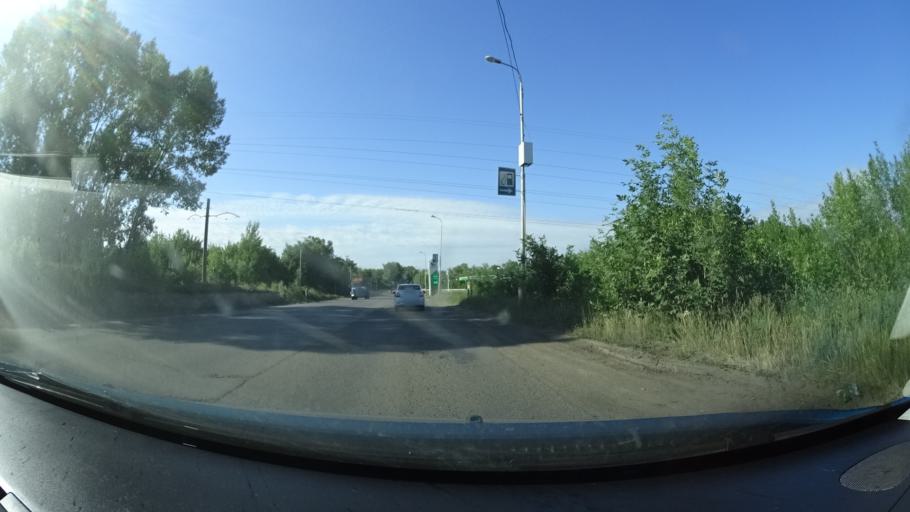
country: RU
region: Bashkortostan
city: Ufa
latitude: 54.8479
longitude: 56.0766
